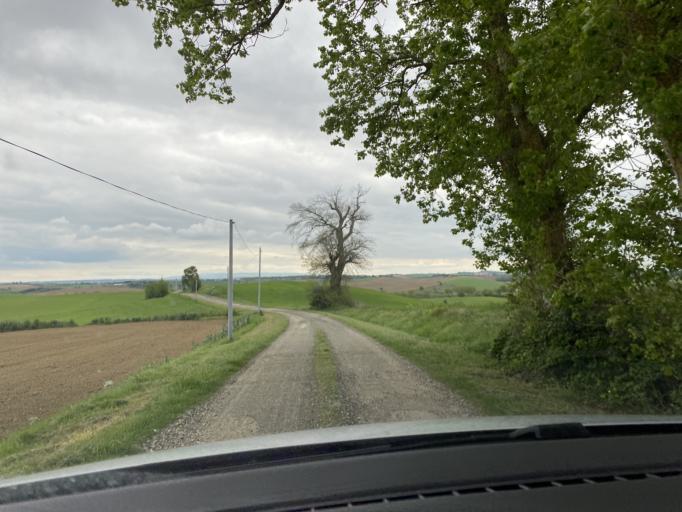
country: FR
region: Midi-Pyrenees
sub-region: Departement de la Haute-Garonne
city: Nailloux
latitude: 43.3631
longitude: 1.6347
